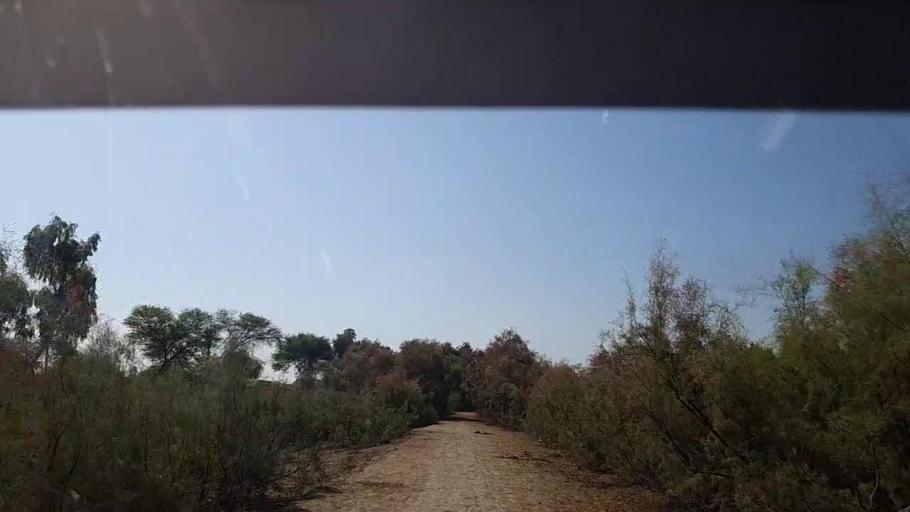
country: PK
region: Sindh
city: Ghauspur
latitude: 28.1799
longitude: 69.0281
